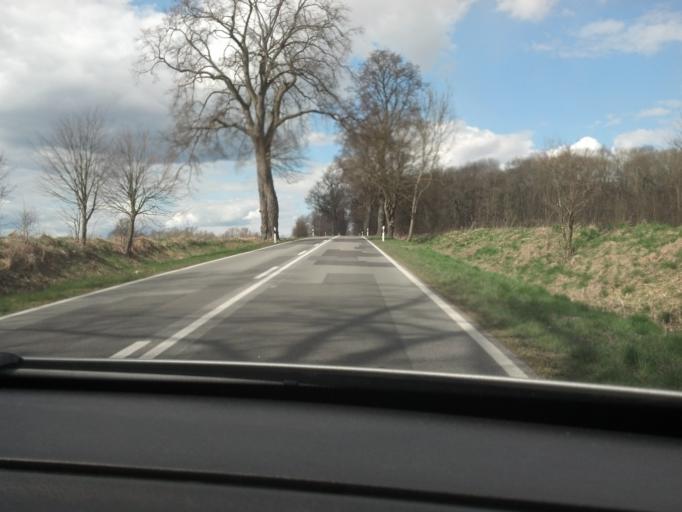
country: DE
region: Mecklenburg-Vorpommern
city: Burg Stargard
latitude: 53.4731
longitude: 13.3476
